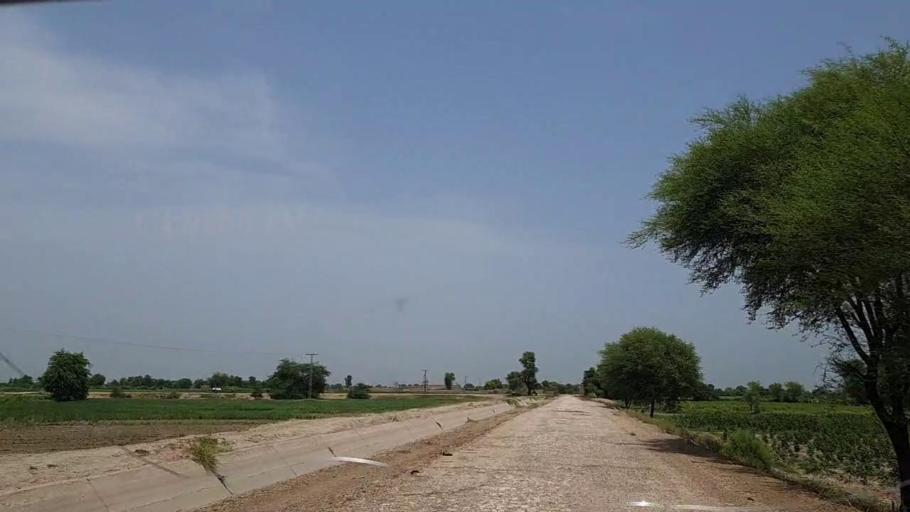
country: PK
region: Sindh
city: Tharu Shah
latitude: 26.9252
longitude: 68.0675
